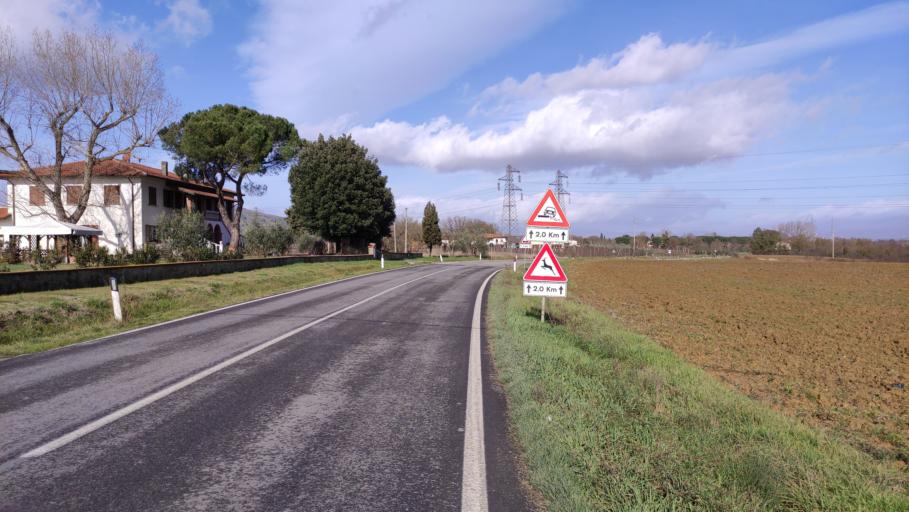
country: IT
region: Tuscany
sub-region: Province of Arezzo
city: Pieve al Toppo
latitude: 43.4246
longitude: 11.7946
